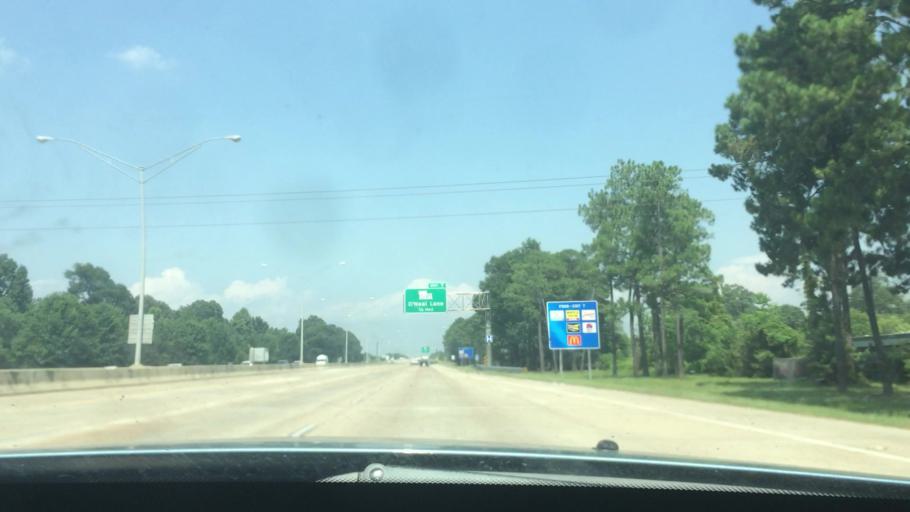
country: US
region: Louisiana
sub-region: East Baton Rouge Parish
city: Shenandoah
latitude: 30.4397
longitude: -91.0179
